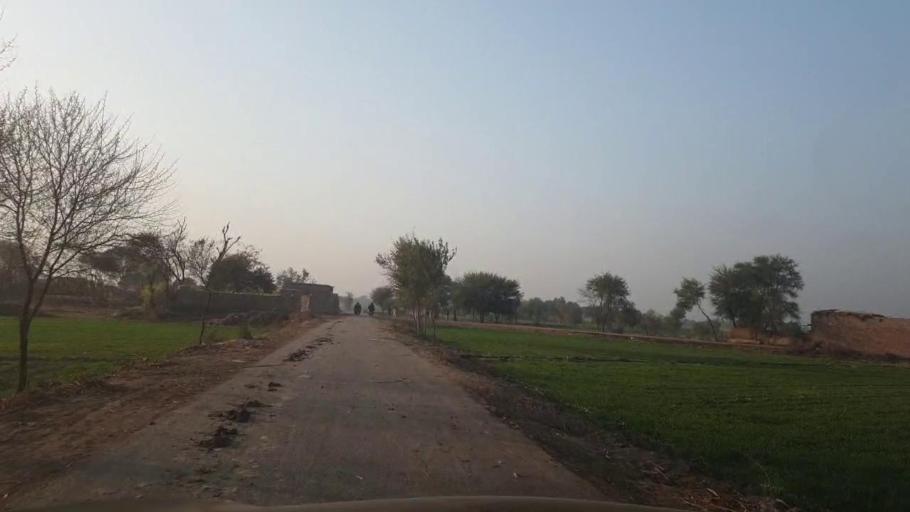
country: PK
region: Sindh
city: Ubauro
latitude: 28.3321
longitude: 69.7711
